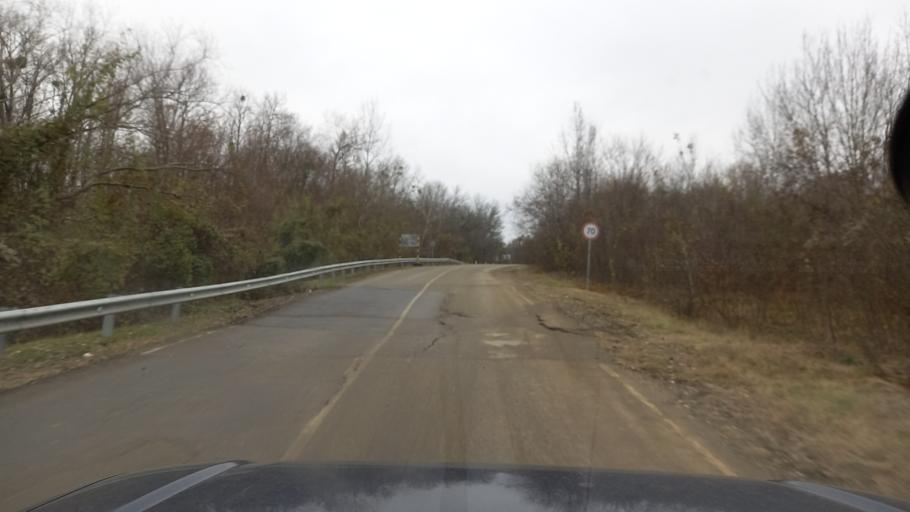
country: RU
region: Krasnodarskiy
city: Goryachiy Klyuch
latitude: 44.5532
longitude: 39.2518
